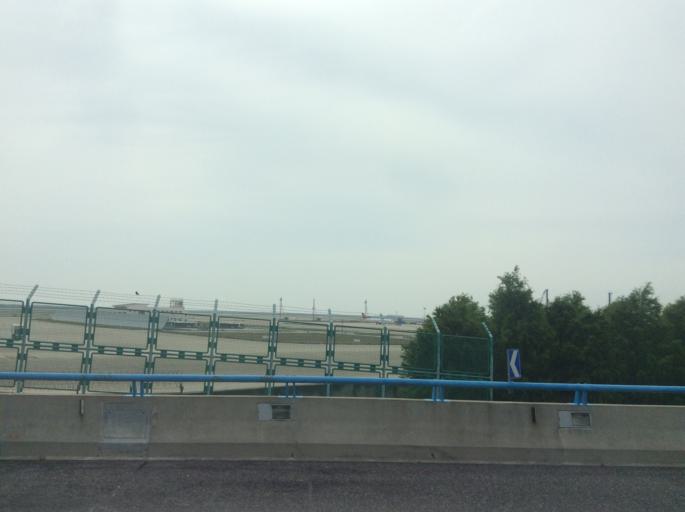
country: CN
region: Shanghai Shi
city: Laogang
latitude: 31.1463
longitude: 121.8058
